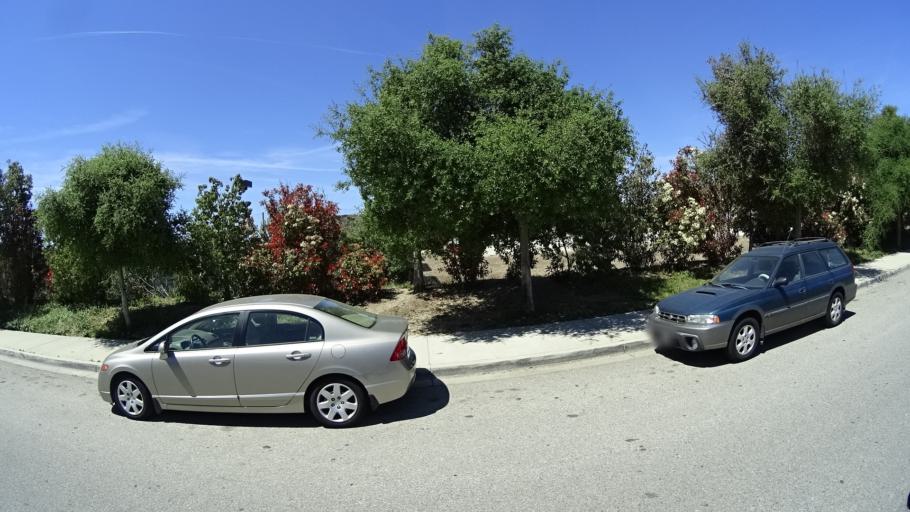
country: US
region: California
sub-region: Ventura County
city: Moorpark
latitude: 34.2279
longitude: -118.8757
